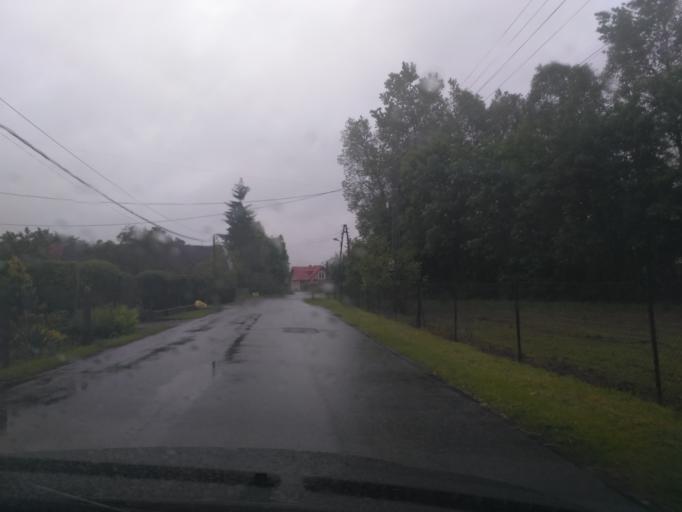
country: PL
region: Subcarpathian Voivodeship
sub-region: Powiat jasielski
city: Jaslo
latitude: 49.7409
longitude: 21.5022
